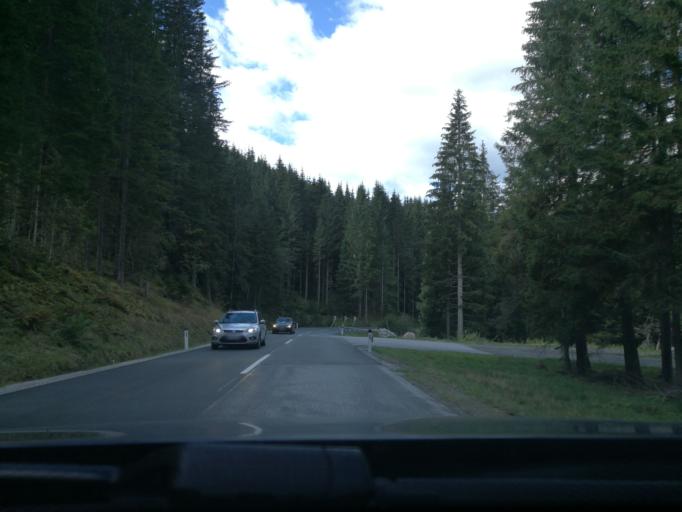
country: AT
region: Tyrol
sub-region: Politischer Bezirk Schwaz
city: Gerlos
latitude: 47.2366
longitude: 12.0672
